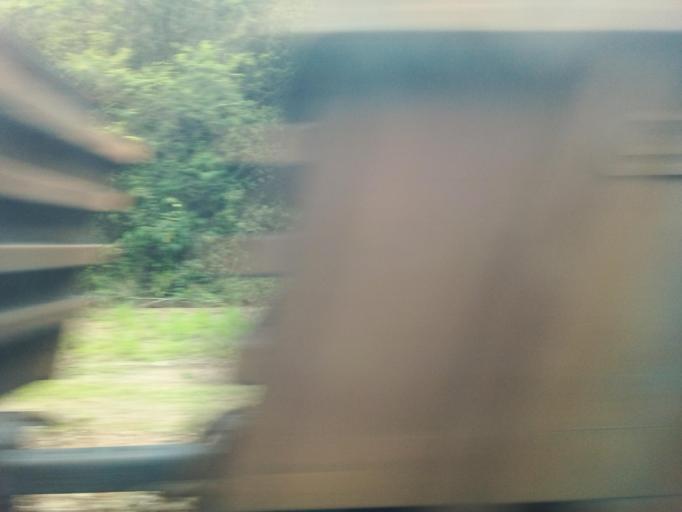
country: BR
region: Minas Gerais
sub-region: Rio Piracicaba
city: Rio Piracicaba
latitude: -19.9683
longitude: -43.2568
